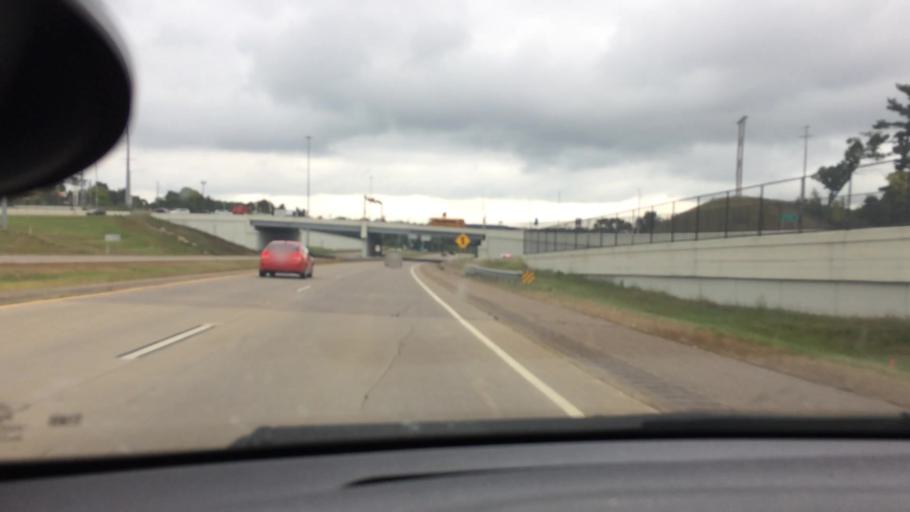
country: US
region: Wisconsin
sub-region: Eau Claire County
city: Altoona
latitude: 44.7931
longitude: -91.4552
